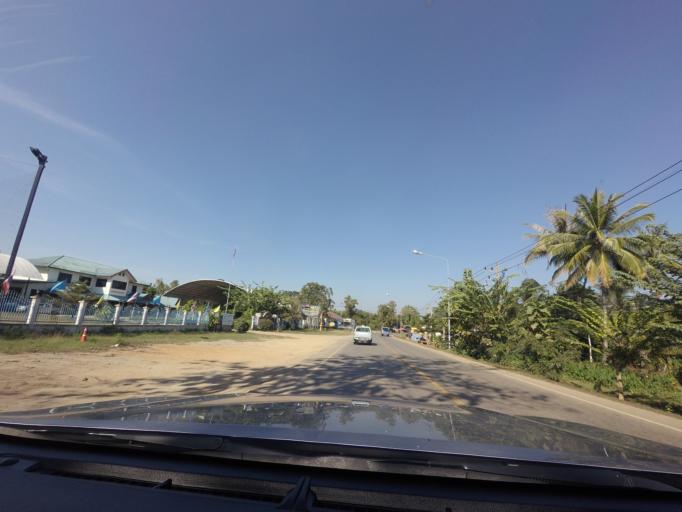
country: TH
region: Sukhothai
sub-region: Amphoe Si Satchanalai
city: Si Satchanalai
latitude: 17.6711
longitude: 99.6929
